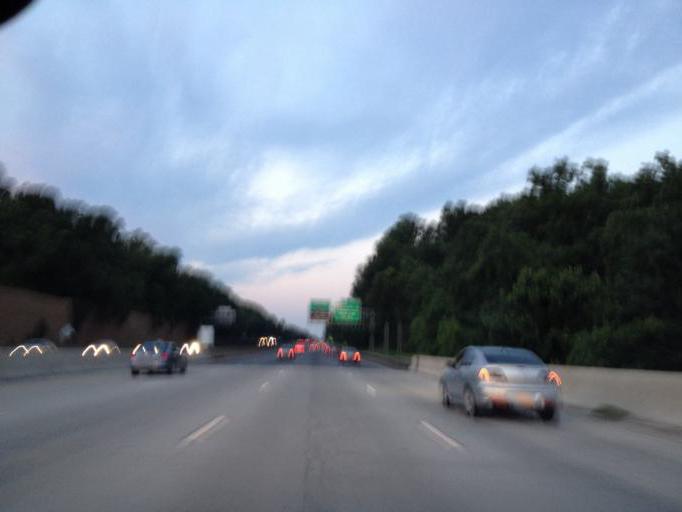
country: US
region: Maryland
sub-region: Montgomery County
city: Four Corners
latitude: 39.0175
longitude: -76.9939
